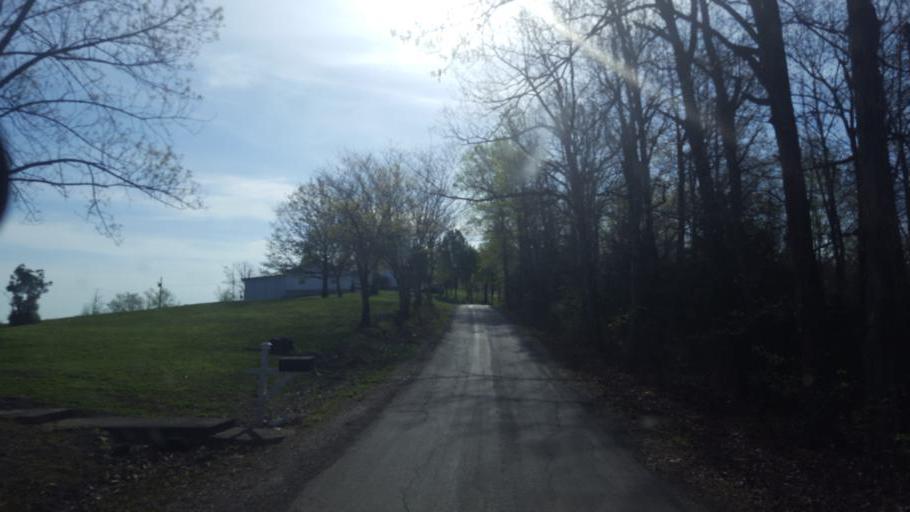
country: US
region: Kentucky
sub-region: Hart County
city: Munfordville
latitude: 37.3273
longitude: -86.0991
